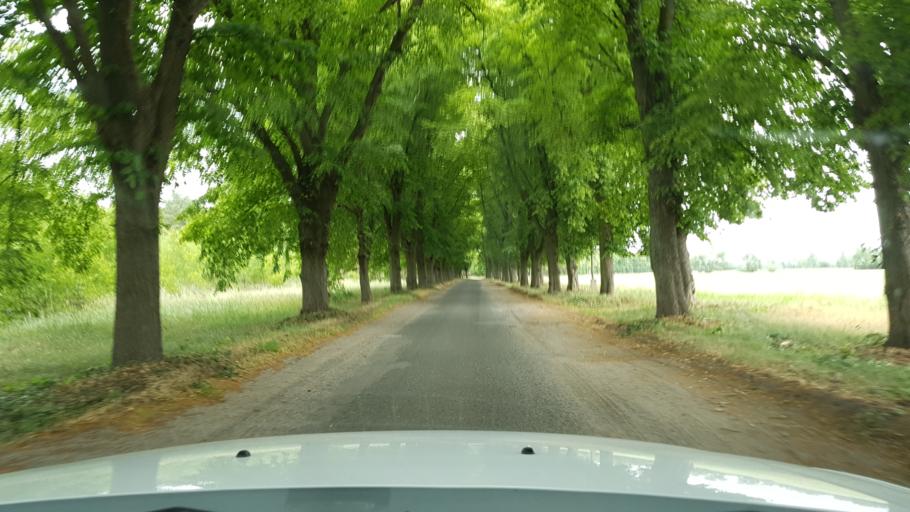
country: DE
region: Brandenburg
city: Manschnow
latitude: 52.6338
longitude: 14.5593
